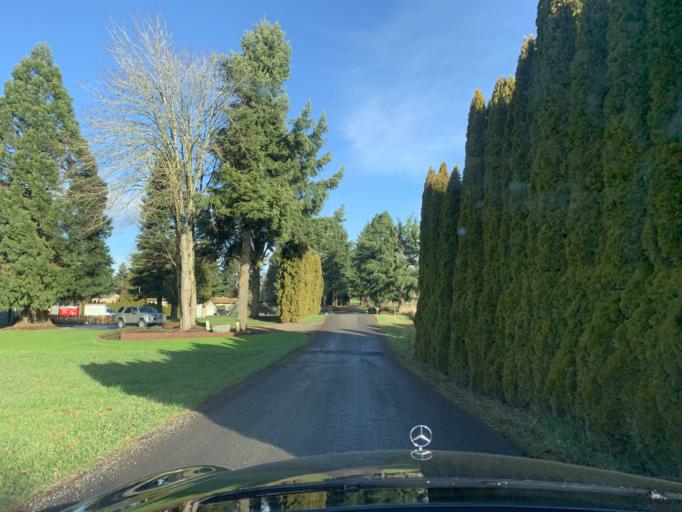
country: US
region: Washington
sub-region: Clark County
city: Five Corners
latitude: 45.7085
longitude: -122.5738
